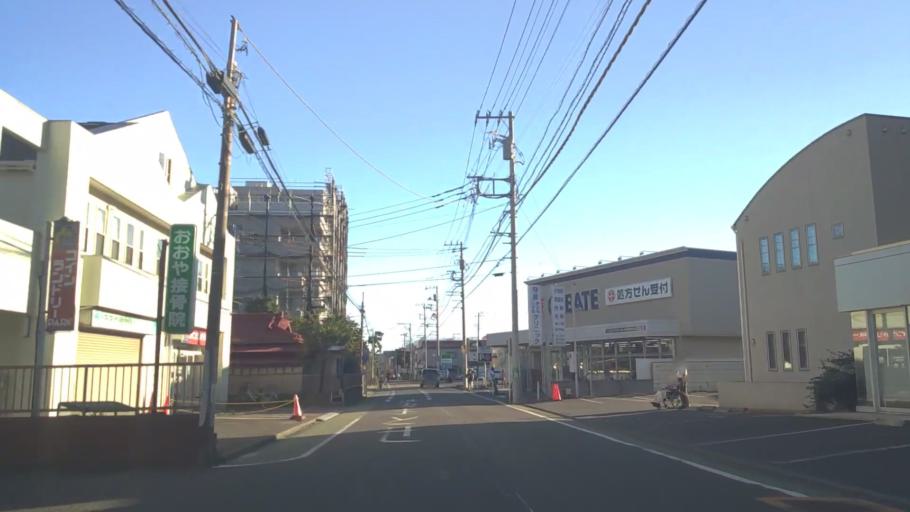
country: JP
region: Kanagawa
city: Chigasaki
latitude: 35.3305
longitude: 139.4145
